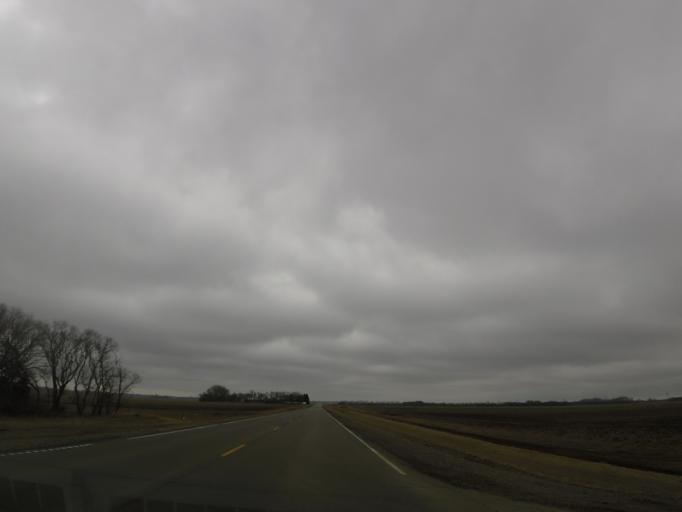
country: US
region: North Dakota
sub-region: Cass County
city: Horace
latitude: 46.6298
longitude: -97.0958
